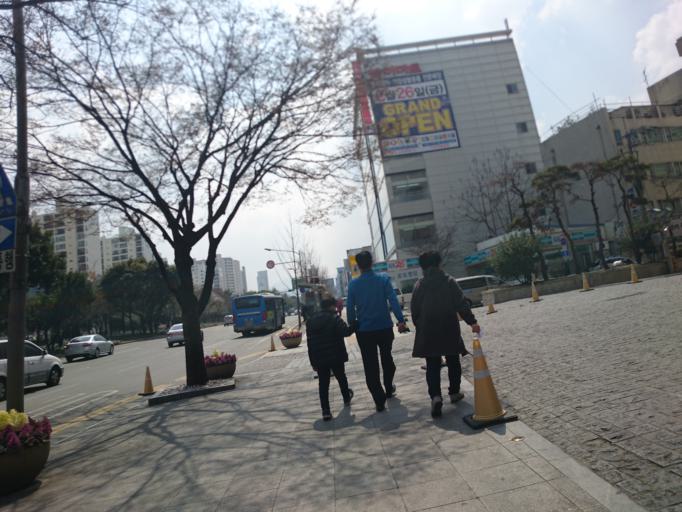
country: KR
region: Daegu
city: Daegu
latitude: 35.8577
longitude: 128.6256
